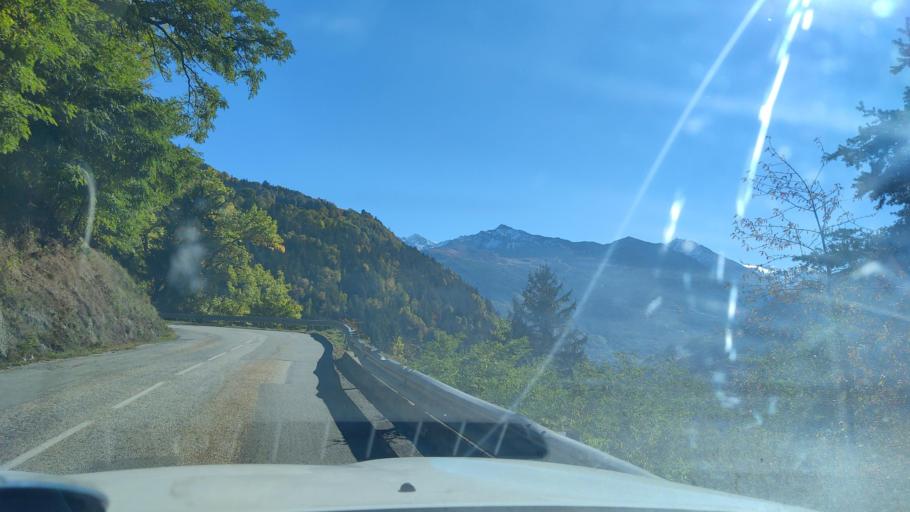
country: FR
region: Rhone-Alpes
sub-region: Departement de la Savoie
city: Seez
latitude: 45.6181
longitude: 6.8258
